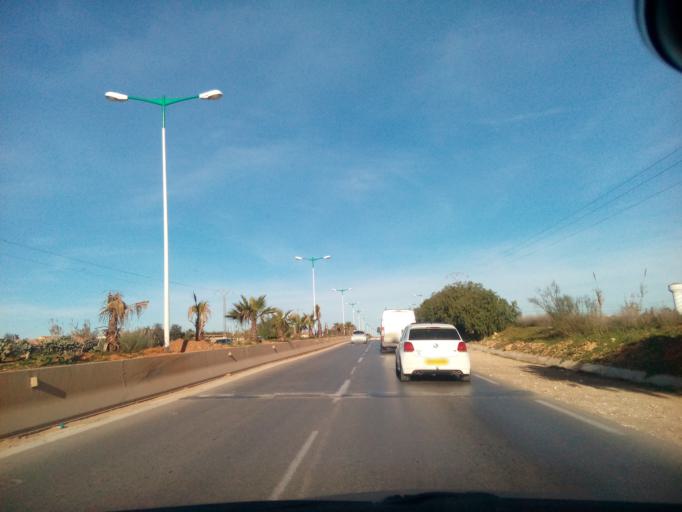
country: DZ
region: Mostaganem
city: Mostaganem
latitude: 35.8684
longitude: 0.1515
